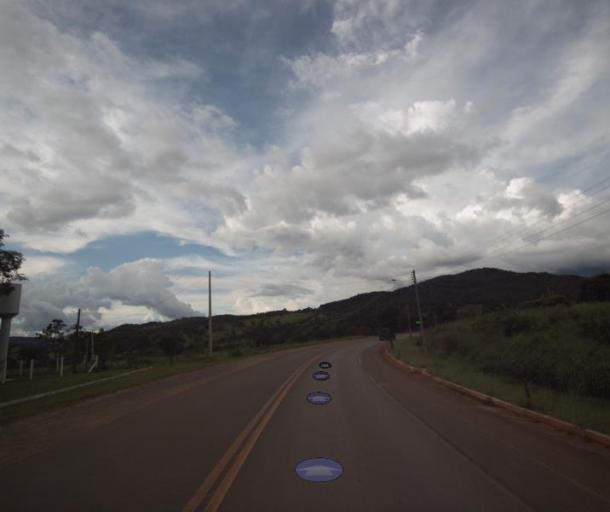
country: BR
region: Goias
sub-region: Niquelandia
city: Niquelandia
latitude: -14.4721
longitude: -48.4885
